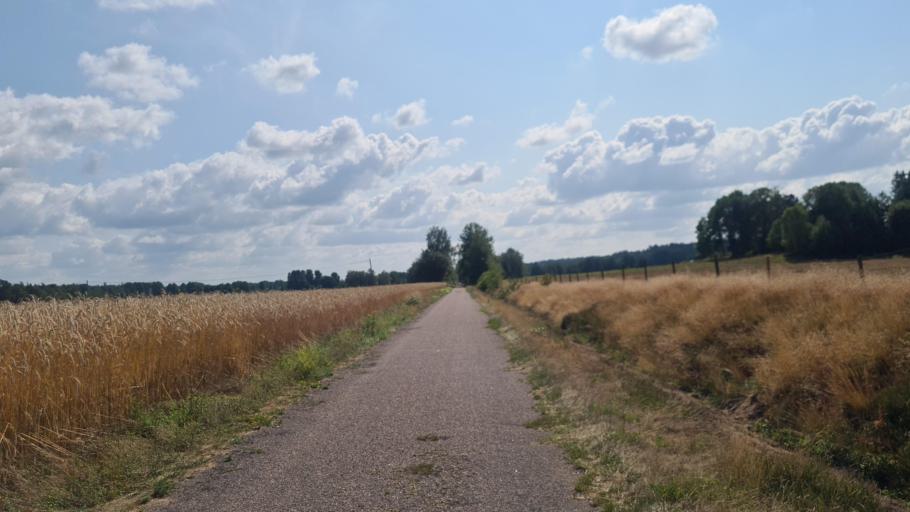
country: SE
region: Kronoberg
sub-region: Ljungby Kommun
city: Ljungby
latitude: 56.7992
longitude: 13.9123
